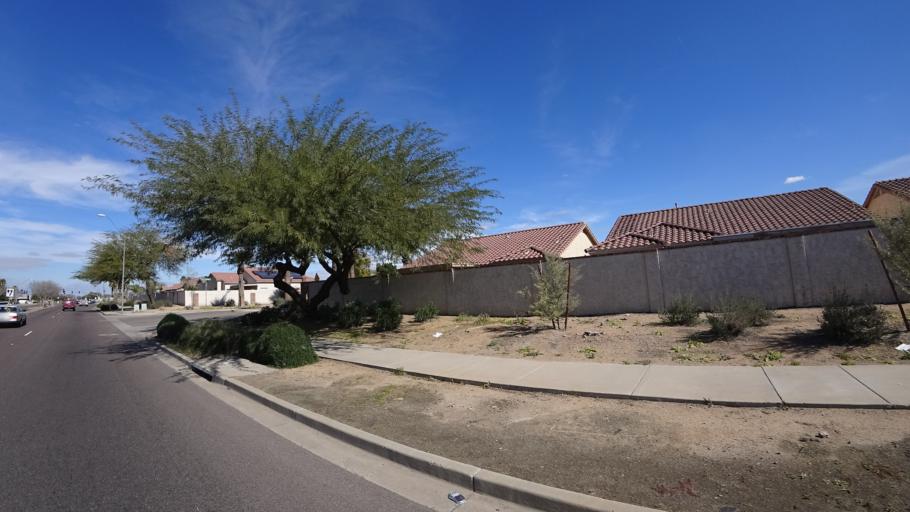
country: US
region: Arizona
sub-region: Maricopa County
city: Peoria
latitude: 33.6226
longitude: -112.2024
